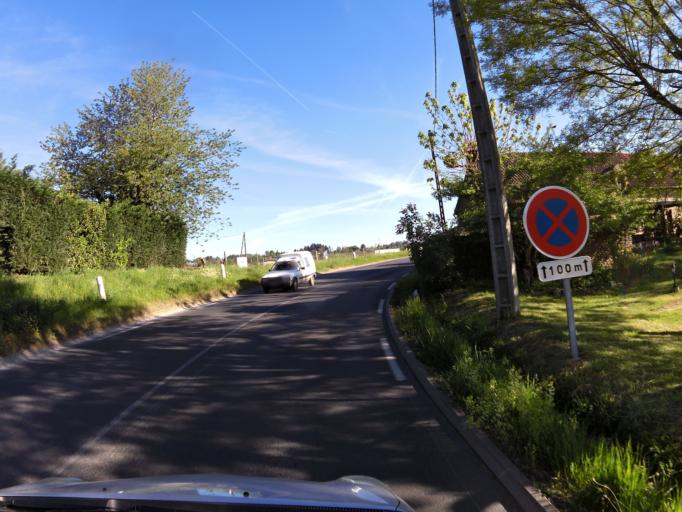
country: FR
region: Aquitaine
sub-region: Departement de la Dordogne
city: Sarlat-la-Caneda
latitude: 44.9283
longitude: 1.2050
